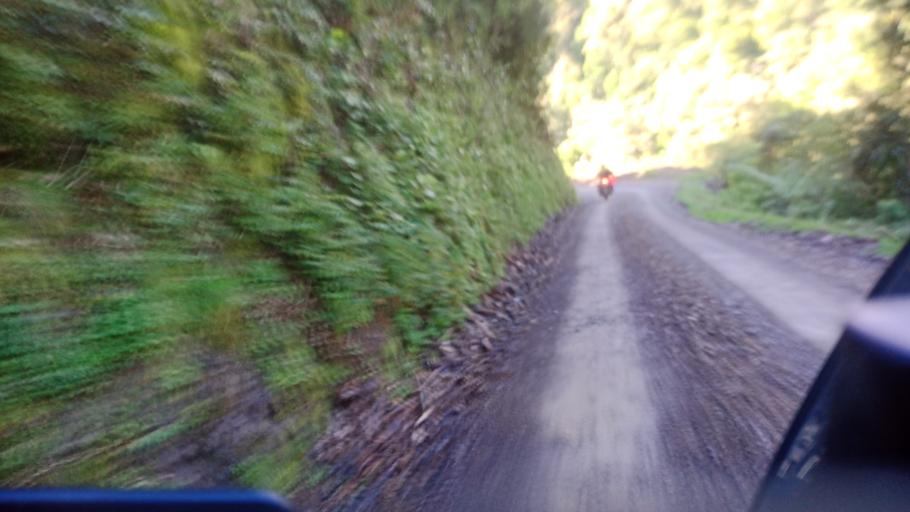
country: NZ
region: Bay of Plenty
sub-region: Opotiki District
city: Opotiki
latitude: -38.0808
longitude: 177.4763
